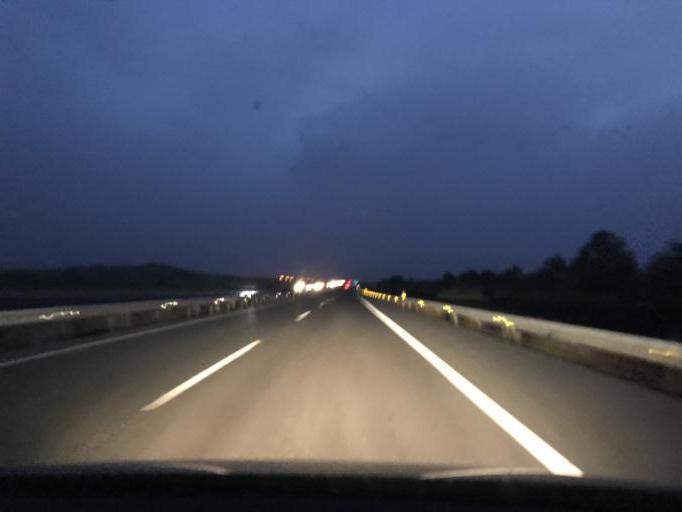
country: ES
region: Andalusia
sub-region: Provincia de Granada
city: Gor
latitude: 37.3869
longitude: -3.0480
